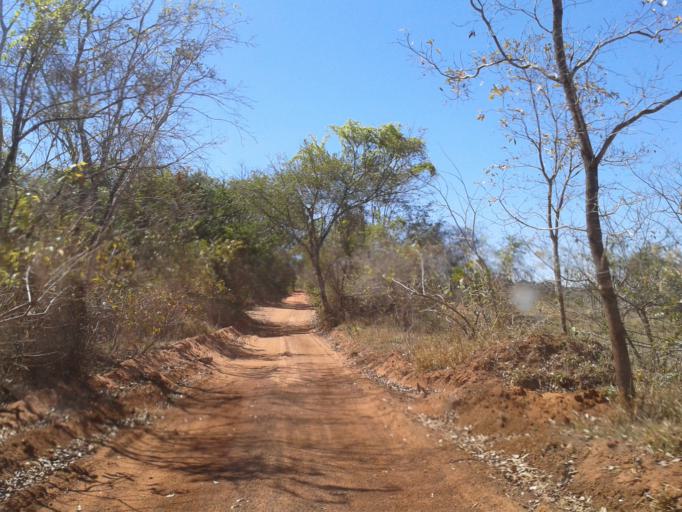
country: BR
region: Minas Gerais
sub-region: Ituiutaba
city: Ituiutaba
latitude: -19.0941
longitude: -49.2972
